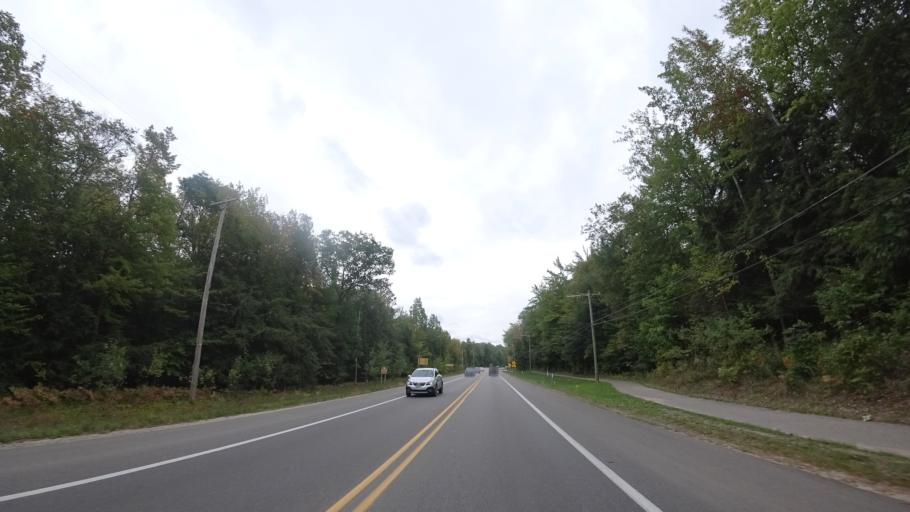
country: US
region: Michigan
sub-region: Emmet County
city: Petoskey
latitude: 45.4126
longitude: -84.9040
